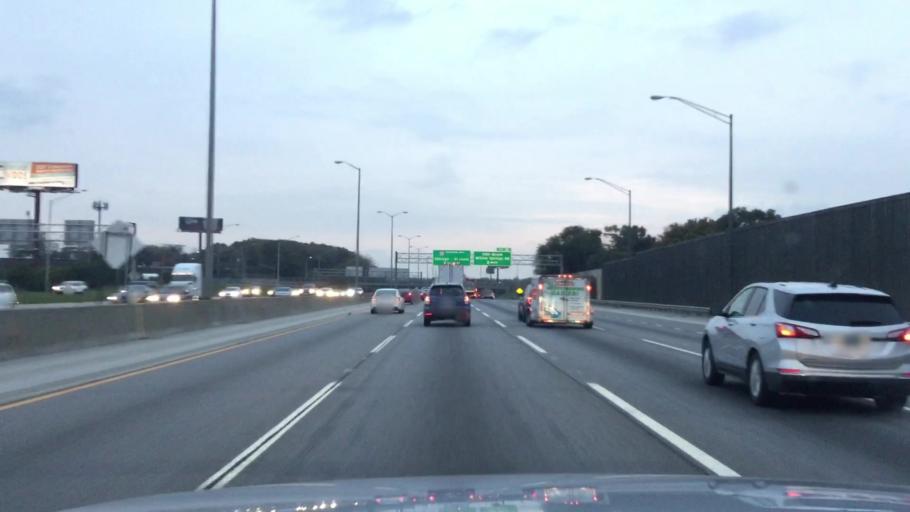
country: US
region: Illinois
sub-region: Cook County
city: Justice
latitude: 41.7429
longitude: -87.8335
